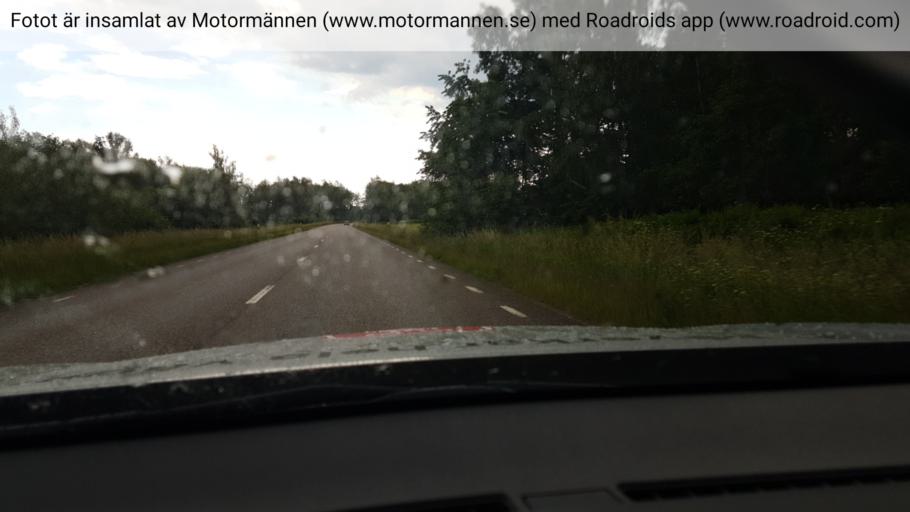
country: SE
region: Vaestra Goetaland
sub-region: Hjo Kommun
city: Hjo
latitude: 58.2978
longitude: 14.2578
